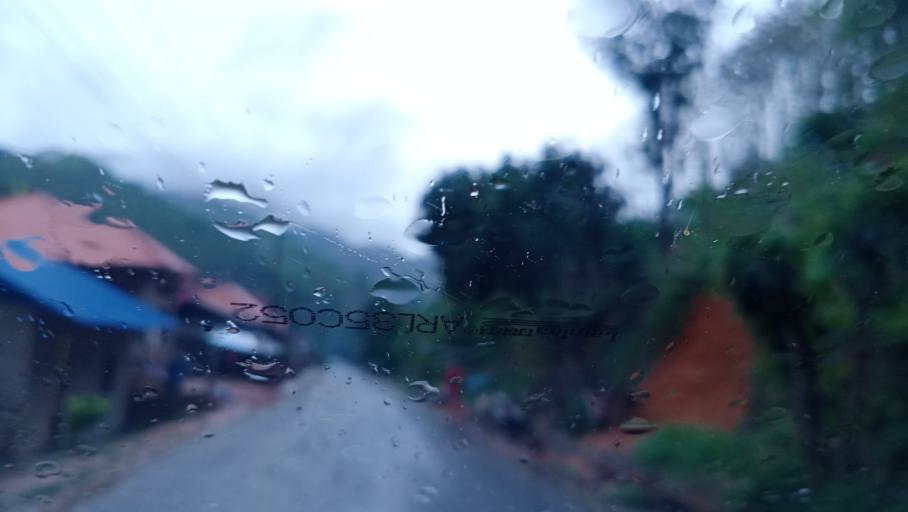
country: LA
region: Phongsali
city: Khoa
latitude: 21.0680
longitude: 102.4900
